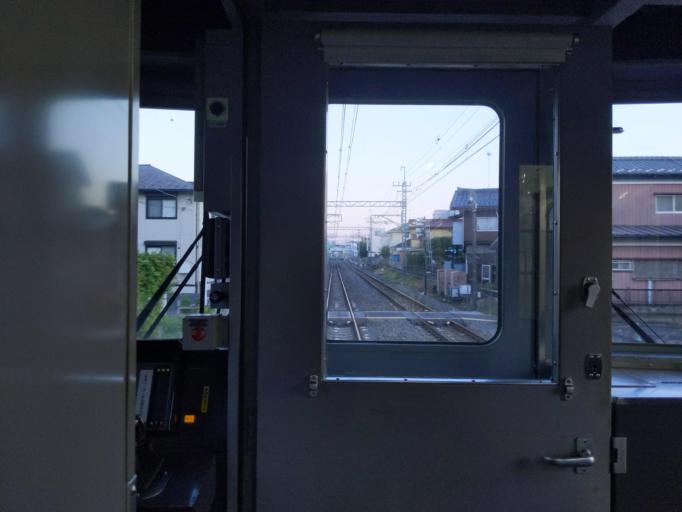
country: JP
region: Chiba
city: Noda
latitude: 35.9341
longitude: 139.8885
